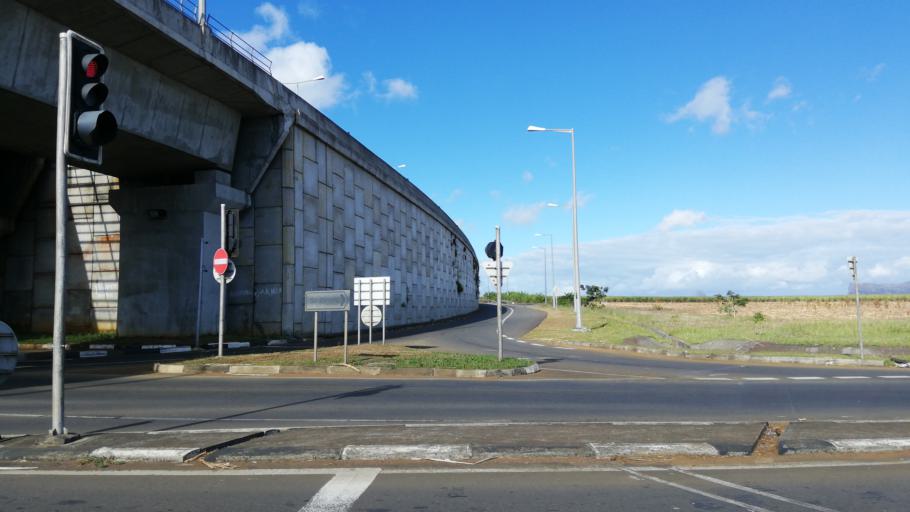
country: MU
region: Moka
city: Verdun
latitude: -20.2286
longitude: 57.5452
